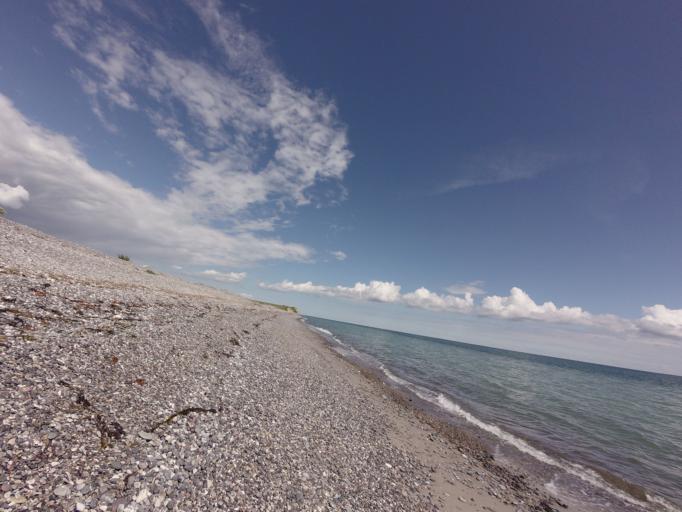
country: DK
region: Central Jutland
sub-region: Norddjurs Kommune
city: Grenaa
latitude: 56.4972
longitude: 10.8699
